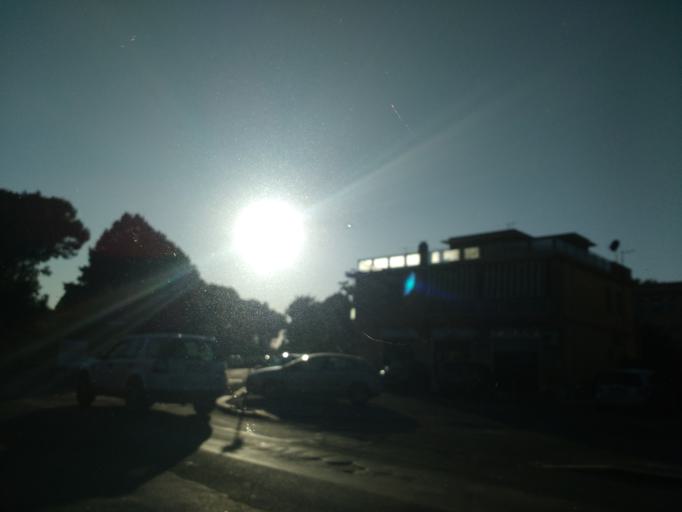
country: IT
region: Latium
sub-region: Citta metropolitana di Roma Capitale
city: Vitinia
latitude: 41.7840
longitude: 12.3677
